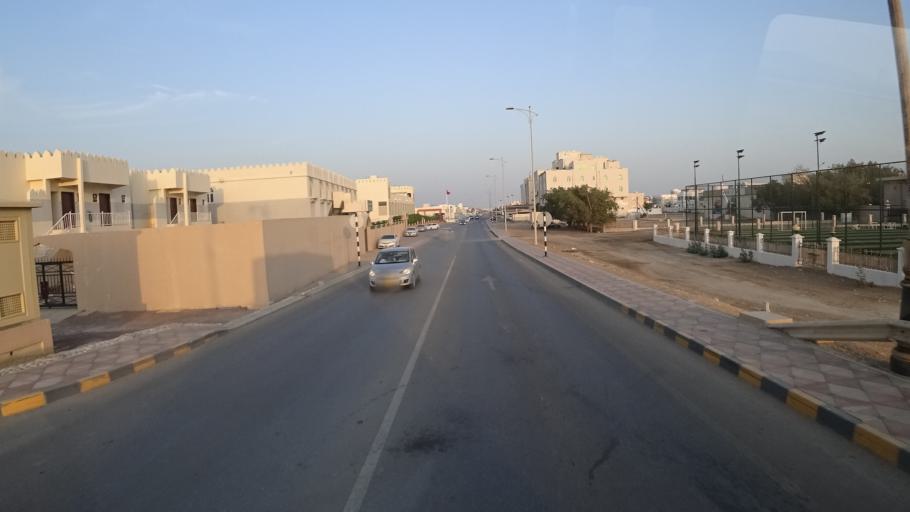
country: OM
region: Ash Sharqiyah
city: Sur
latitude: 22.5961
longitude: 59.4917
